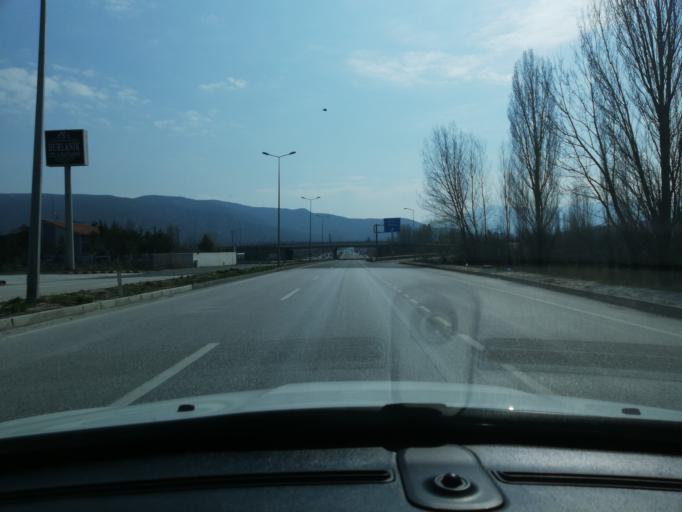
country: TR
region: Cankiri
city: Ilgaz
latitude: 40.9057
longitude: 33.6477
